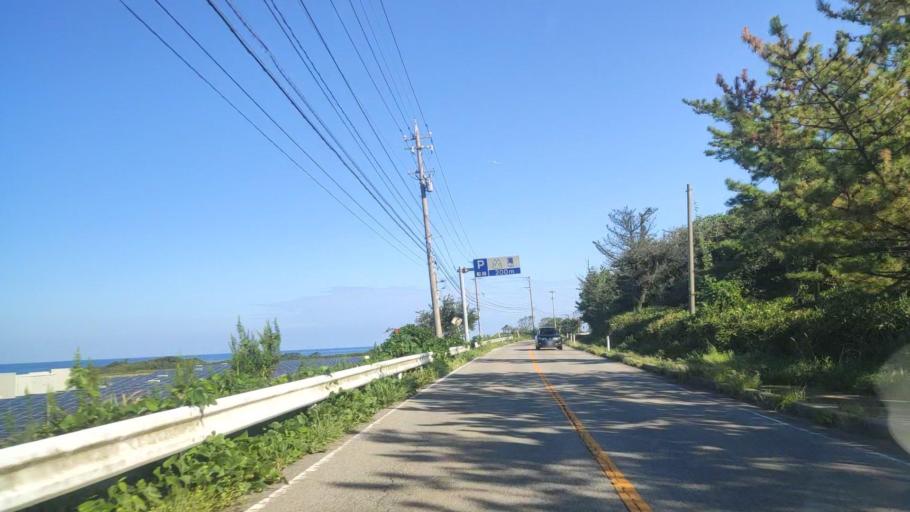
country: JP
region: Ishikawa
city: Hakui
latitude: 36.9304
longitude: 136.7564
